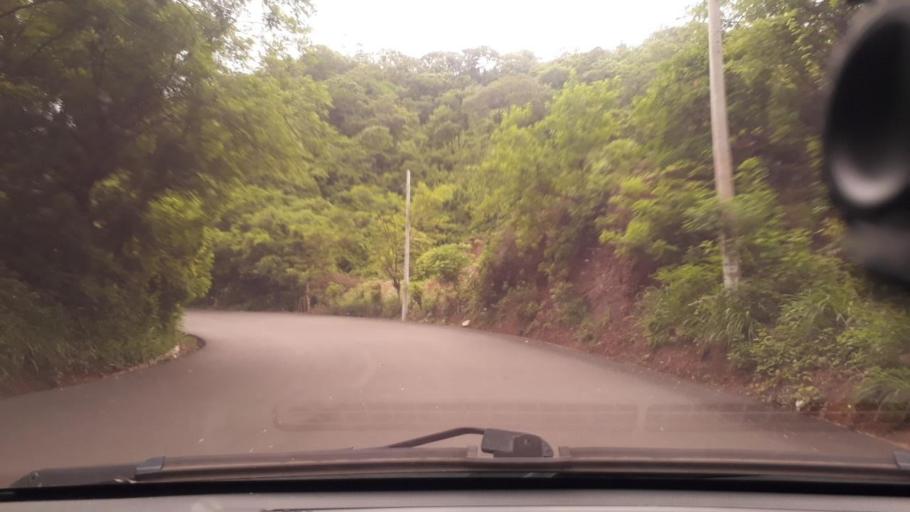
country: GT
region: Chiquimula
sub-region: Municipio de San Juan Ermita
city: San Juan Ermita
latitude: 14.7445
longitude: -89.4652
